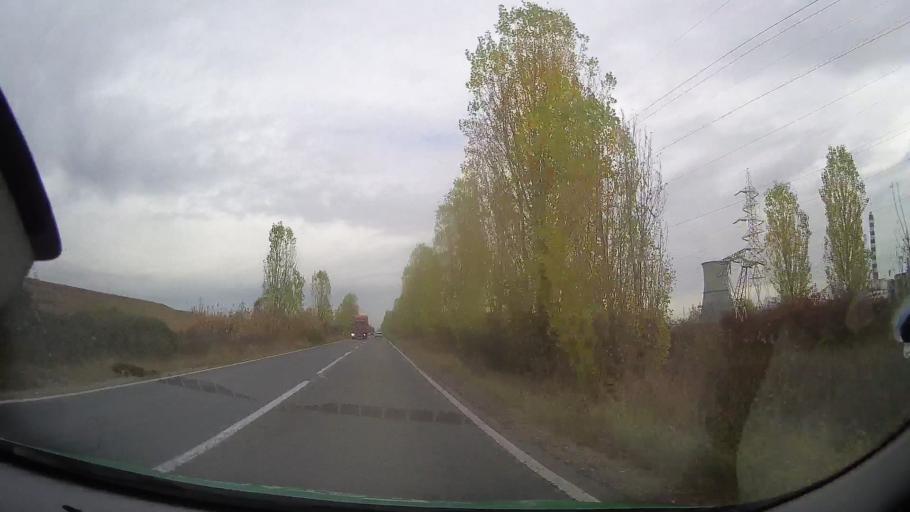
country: RO
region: Prahova
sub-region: Comuna Bucov
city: Bucov
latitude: 44.9544
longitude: 26.0766
